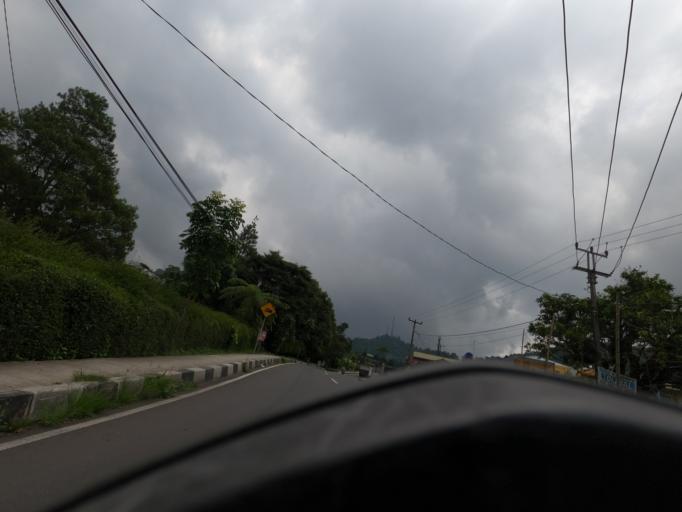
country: ID
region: West Java
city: Caringin
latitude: -6.7109
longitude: 106.9993
